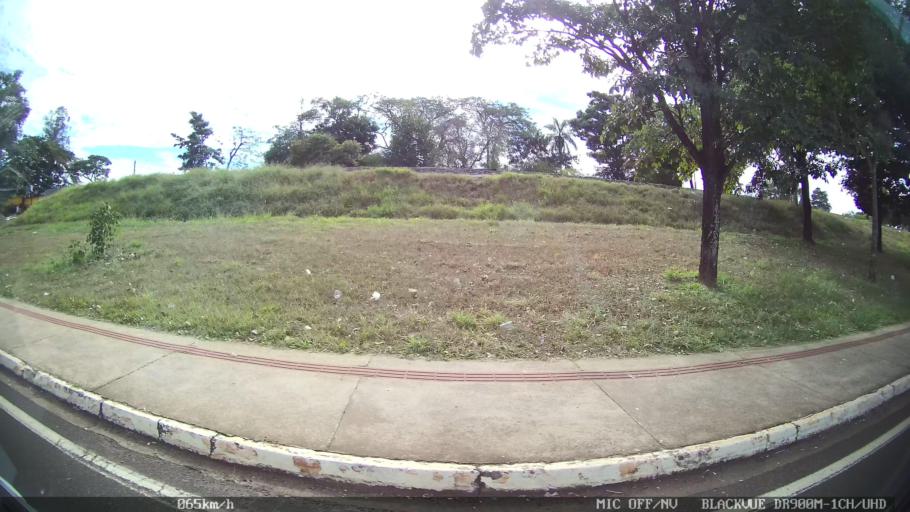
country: BR
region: Sao Paulo
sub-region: Catanduva
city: Catanduva
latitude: -21.1393
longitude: -48.9602
